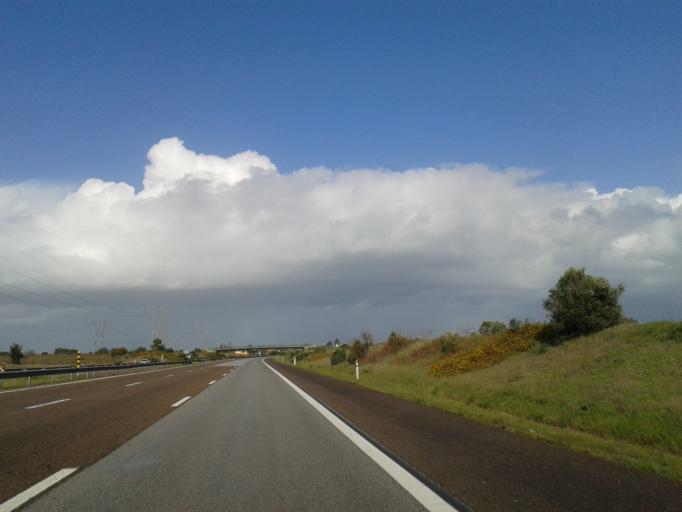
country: PT
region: Setubal
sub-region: Palmela
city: Pinhal Novo
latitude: 38.6136
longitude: -8.8673
